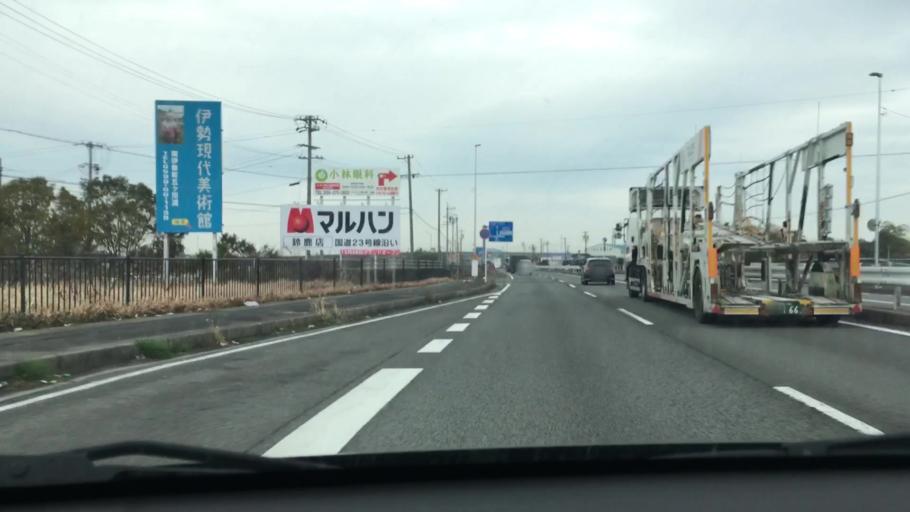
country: JP
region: Mie
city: Suzuka
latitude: 34.8780
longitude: 136.5151
